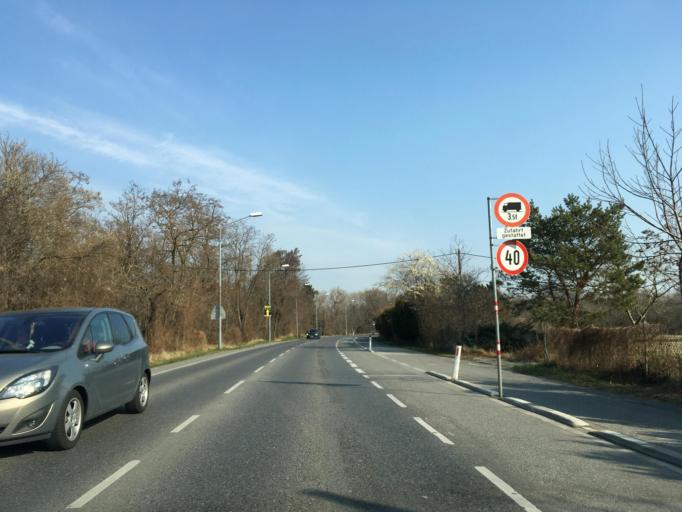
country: AT
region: Lower Austria
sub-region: Politischer Bezirk Wien-Umgebung
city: Schwechat
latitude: 48.1960
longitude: 16.4666
